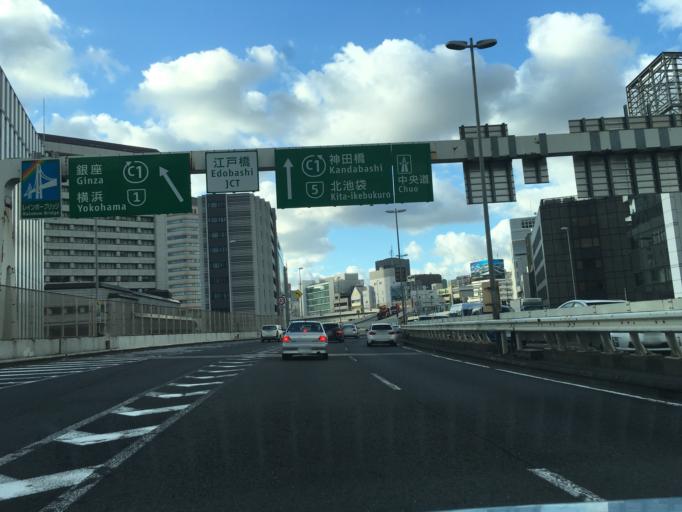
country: JP
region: Tokyo
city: Tokyo
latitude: 35.6815
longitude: 139.7804
